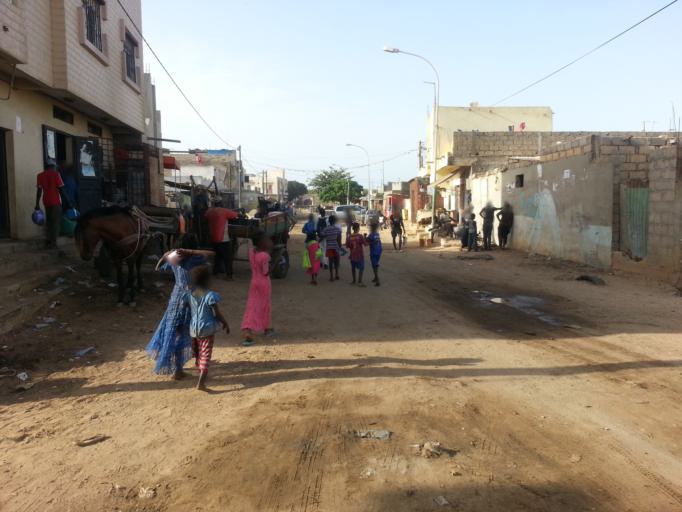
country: SN
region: Dakar
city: Pikine
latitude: 14.7719
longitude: -17.3787
